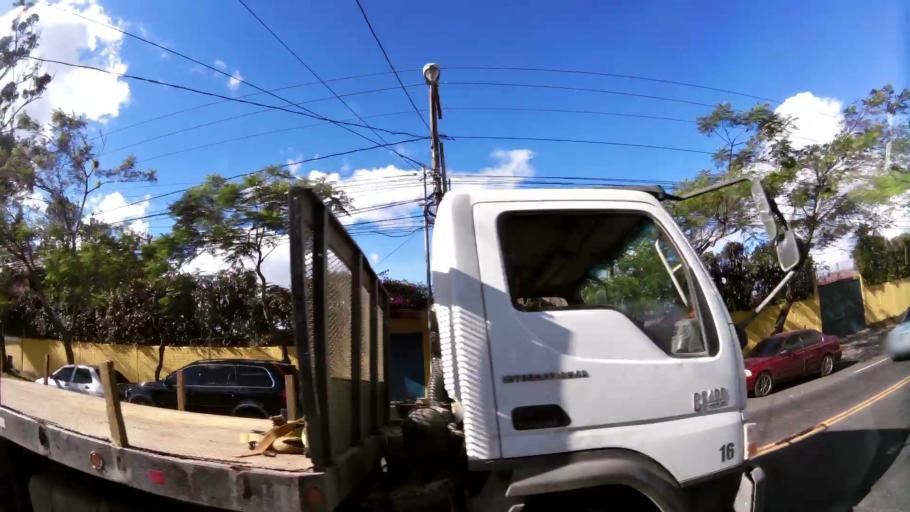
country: GT
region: Guatemala
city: Guatemala City
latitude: 14.6028
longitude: -90.5563
